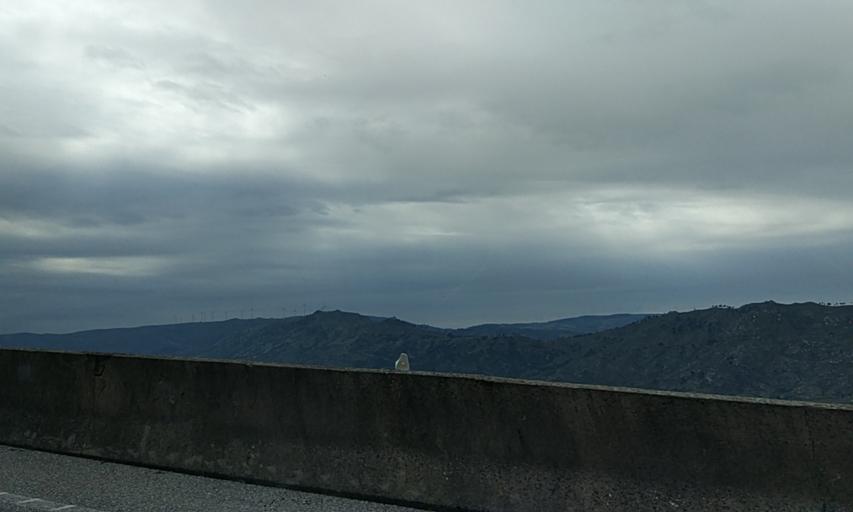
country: PT
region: Guarda
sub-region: Guarda
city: Guarda
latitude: 40.5969
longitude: -7.2757
